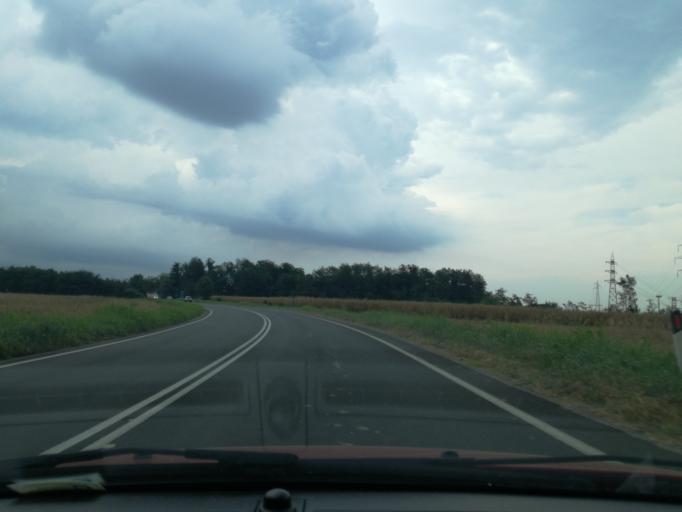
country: IT
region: Lombardy
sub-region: Provincia di Monza e Brianza
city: Velasca
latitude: 45.6389
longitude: 9.3559
